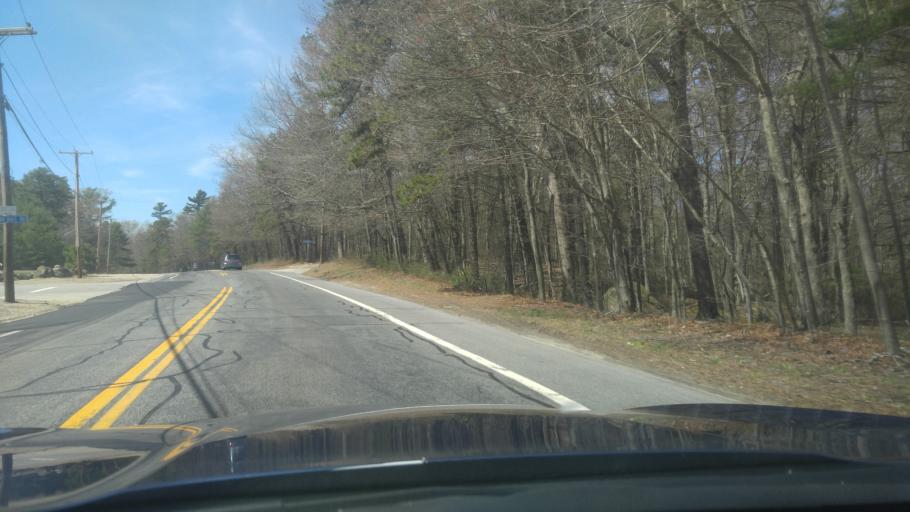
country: US
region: Rhode Island
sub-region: Kent County
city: West Greenwich
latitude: 41.5865
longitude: -71.6186
